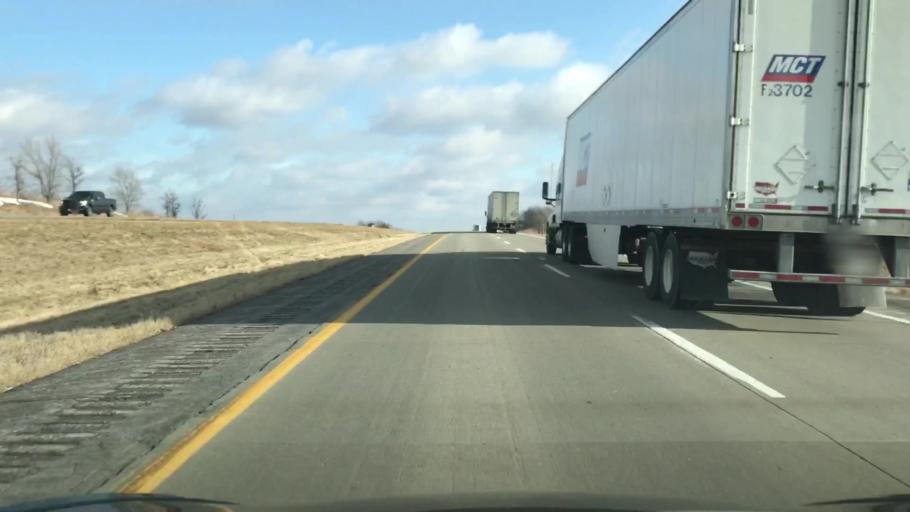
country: US
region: Iowa
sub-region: Cass County
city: Atlantic
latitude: 41.4971
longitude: -94.9705
